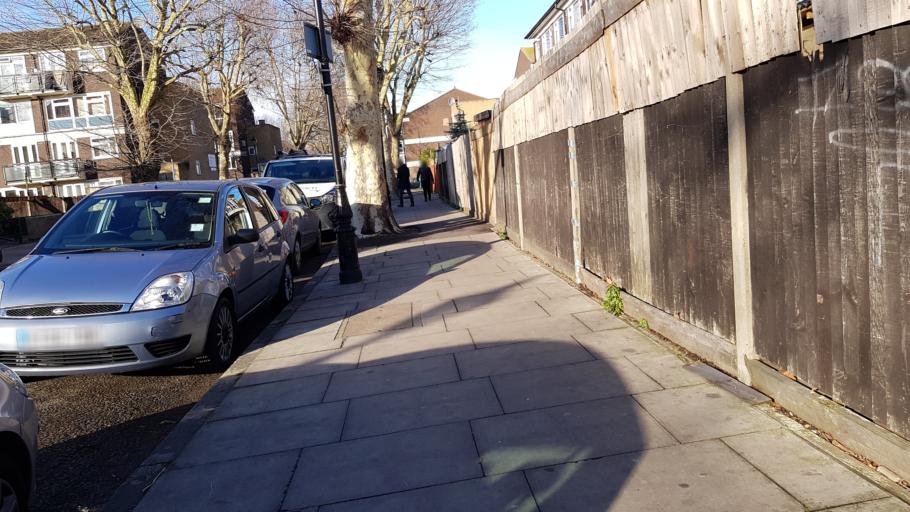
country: GB
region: England
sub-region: Greater London
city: Poplar
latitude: 51.5285
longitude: -0.0236
